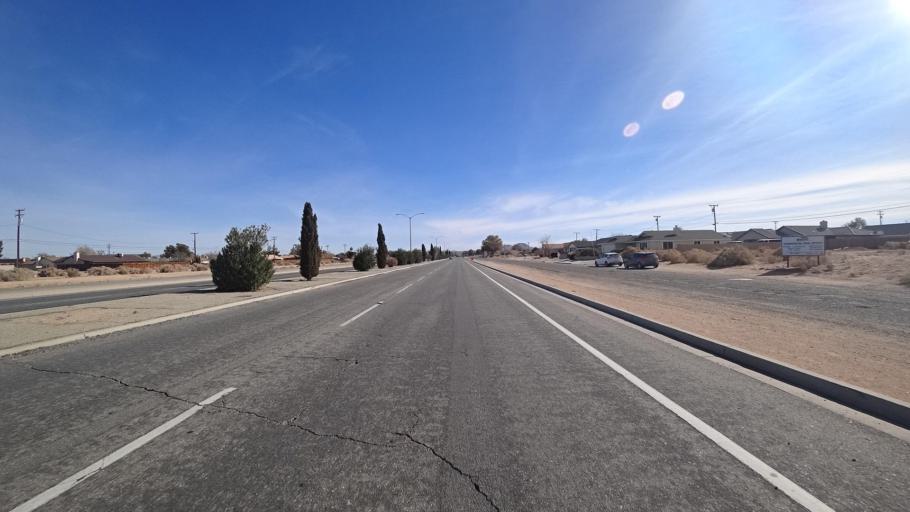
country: US
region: California
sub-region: Kern County
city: California City
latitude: 35.1258
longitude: -117.9652
